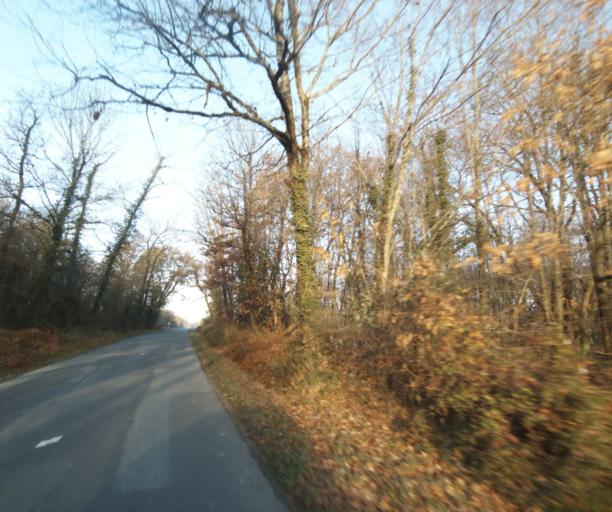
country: FR
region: Poitou-Charentes
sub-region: Departement de la Charente-Maritime
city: Fontcouverte
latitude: 45.7585
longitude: -0.5727
